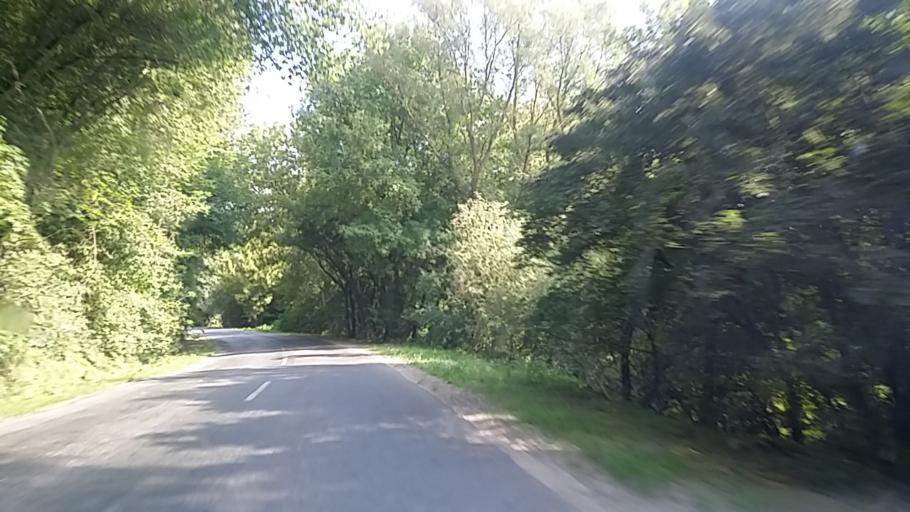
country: HU
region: Tolna
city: Gyonk
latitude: 46.5375
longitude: 18.4974
